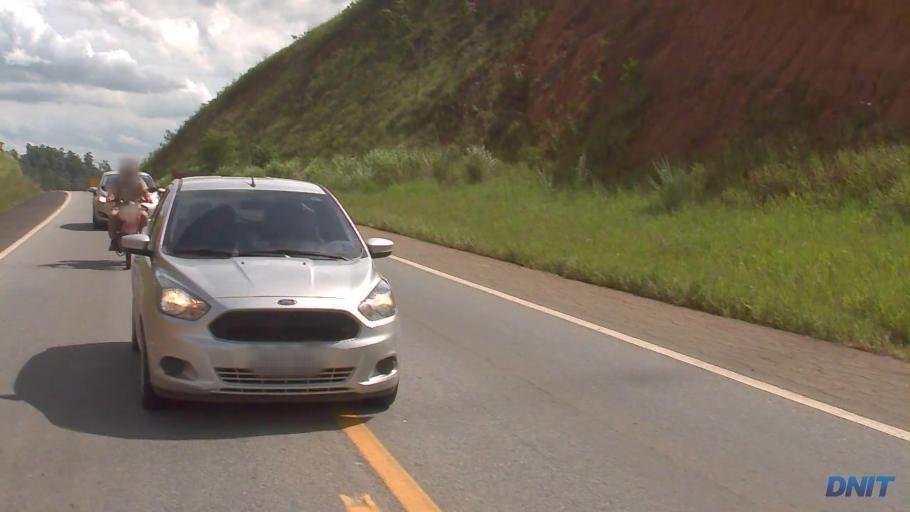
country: BR
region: Minas Gerais
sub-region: Ipatinga
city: Ipatinga
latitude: -19.4180
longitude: -42.4931
